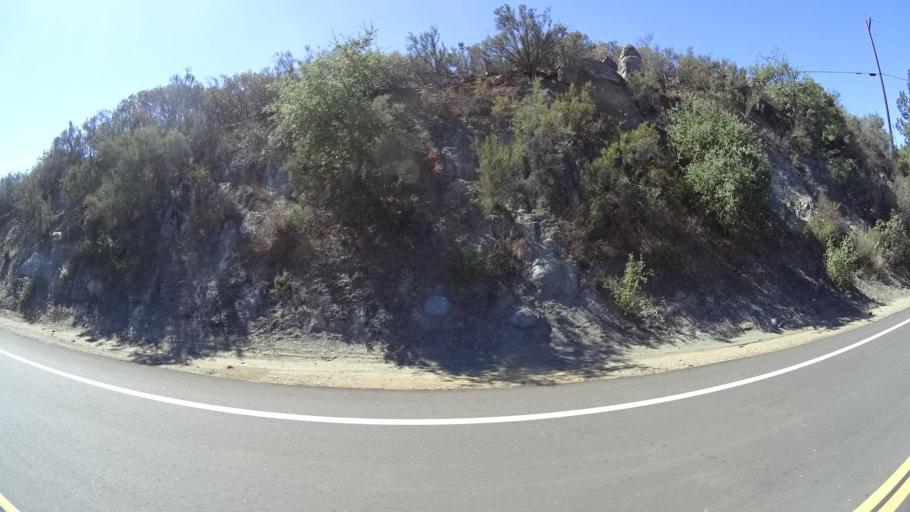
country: US
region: California
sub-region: San Diego County
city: Jamul
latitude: 32.7276
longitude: -116.7779
